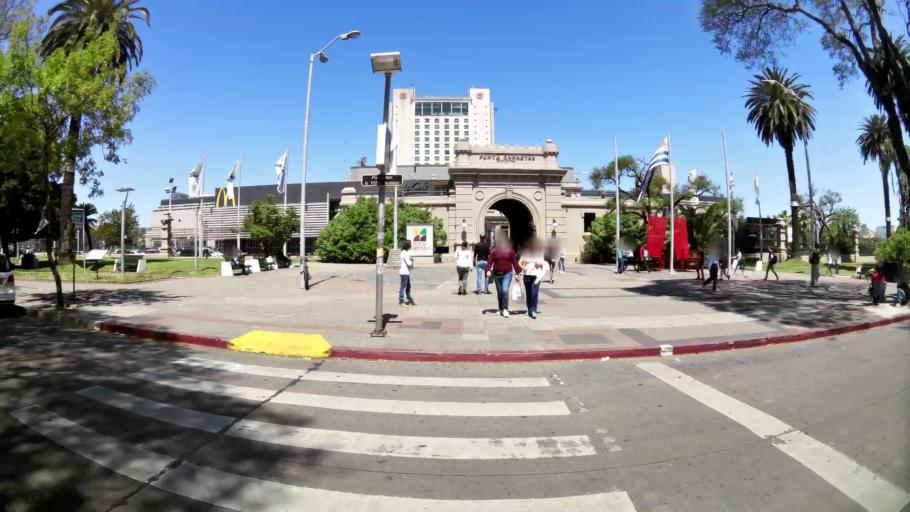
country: UY
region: Montevideo
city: Montevideo
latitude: -34.9235
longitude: -56.1598
